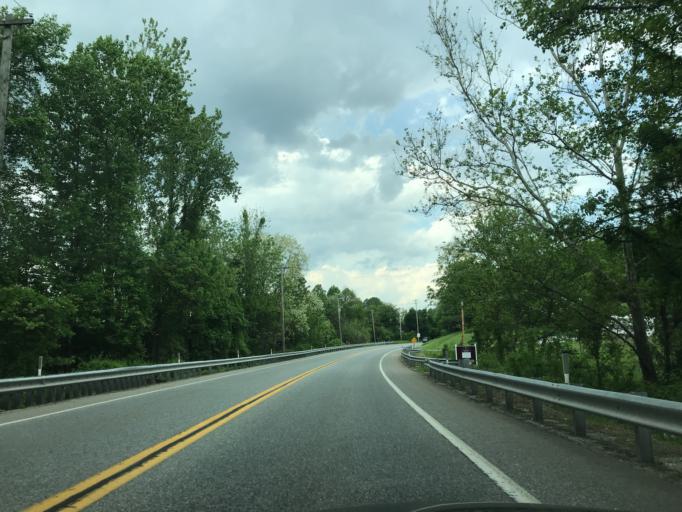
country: US
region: Pennsylvania
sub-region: York County
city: Susquehanna Trails
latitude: 39.7285
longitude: -76.3438
